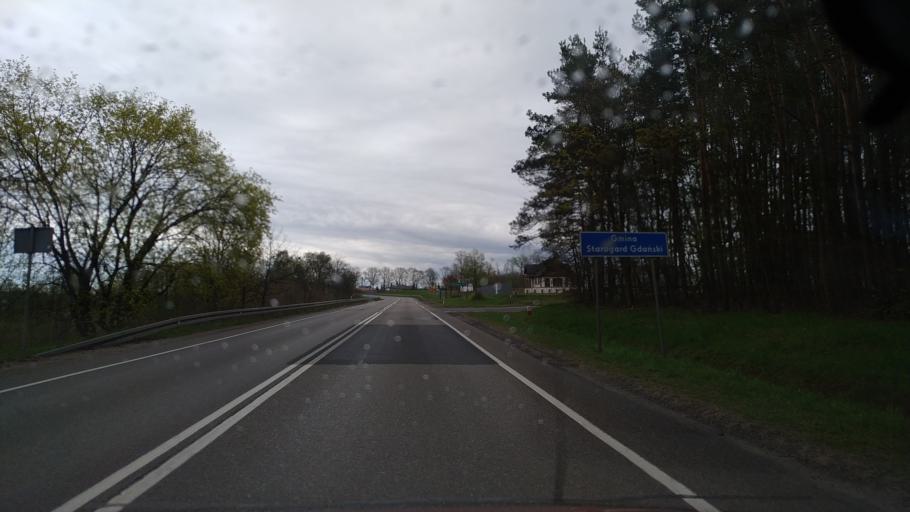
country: PL
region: Pomeranian Voivodeship
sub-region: Powiat starogardzki
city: Lubichowo
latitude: 53.9325
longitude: 18.4059
